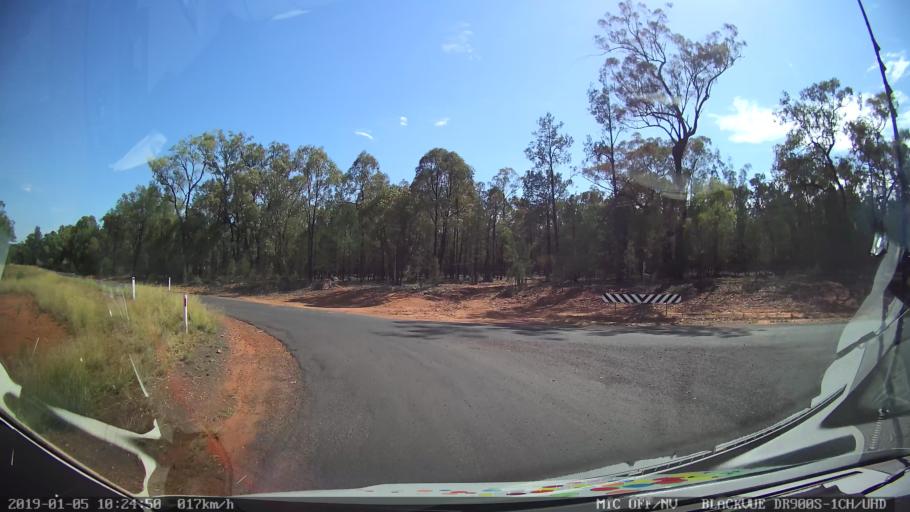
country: AU
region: New South Wales
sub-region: Gilgandra
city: Gilgandra
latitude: -31.5649
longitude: 148.9612
